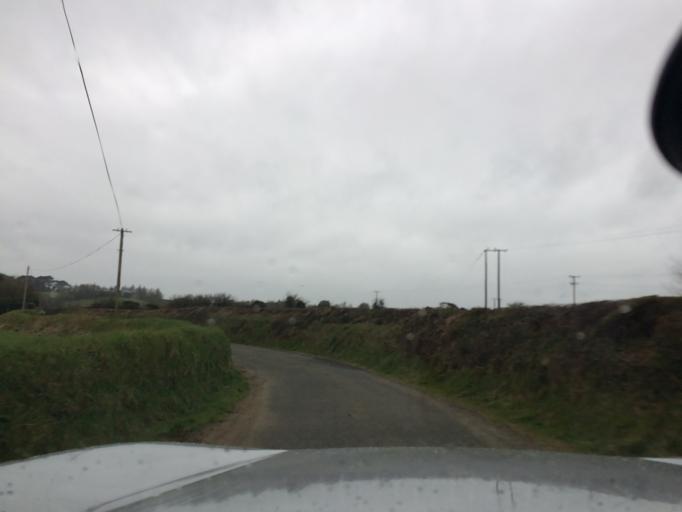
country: IE
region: Munster
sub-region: Waterford
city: Tra Mhor
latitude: 52.2247
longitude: -7.1950
